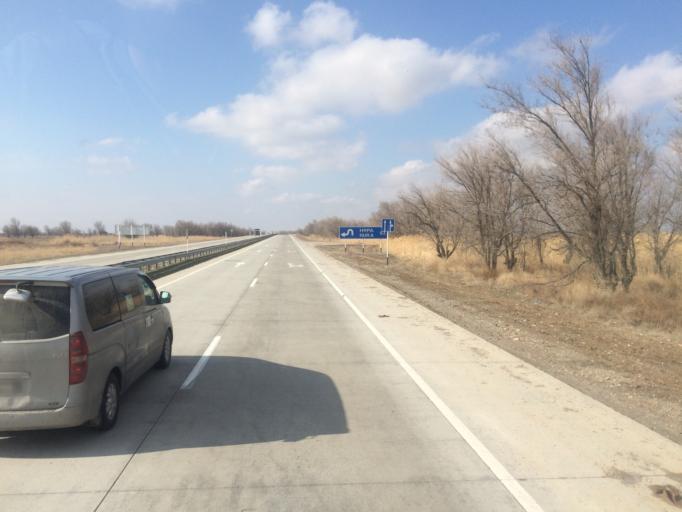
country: KZ
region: Ongtustik Qazaqstan
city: Bayaldyr
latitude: 43.0080
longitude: 68.7754
